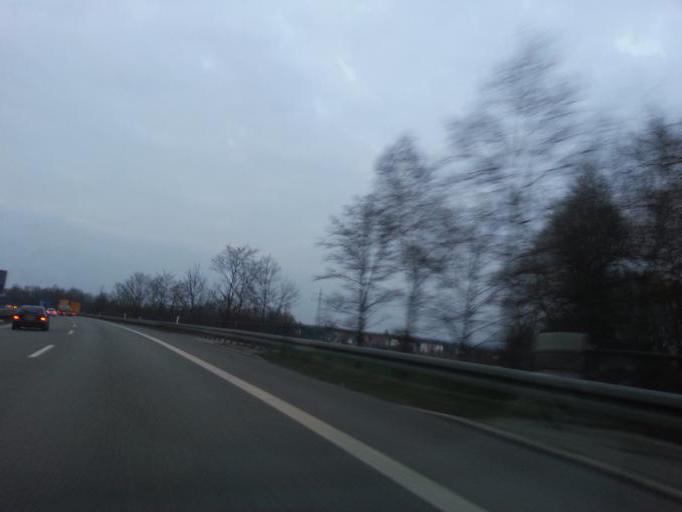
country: DE
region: Baden-Wuerttemberg
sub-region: Tuebingen Region
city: Berg
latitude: 47.8242
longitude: 9.6165
